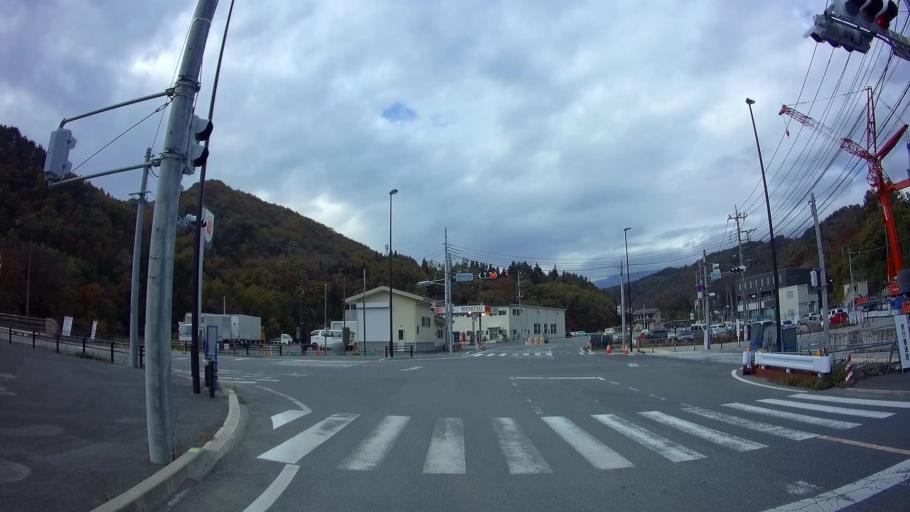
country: JP
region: Gunma
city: Nakanojomachi
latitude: 36.5465
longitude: 138.6477
